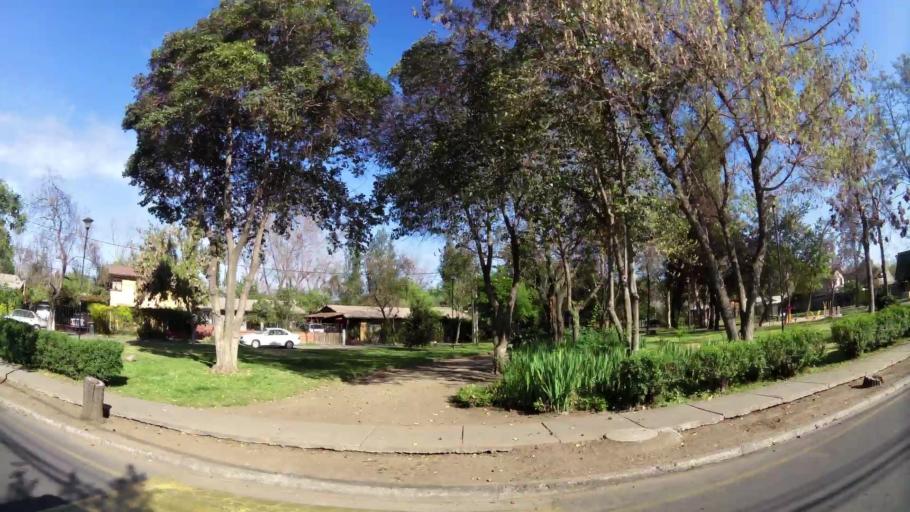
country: CL
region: Santiago Metropolitan
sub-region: Provincia de Santiago
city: Villa Presidente Frei, Nunoa, Santiago, Chile
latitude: -33.4597
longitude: -70.5519
